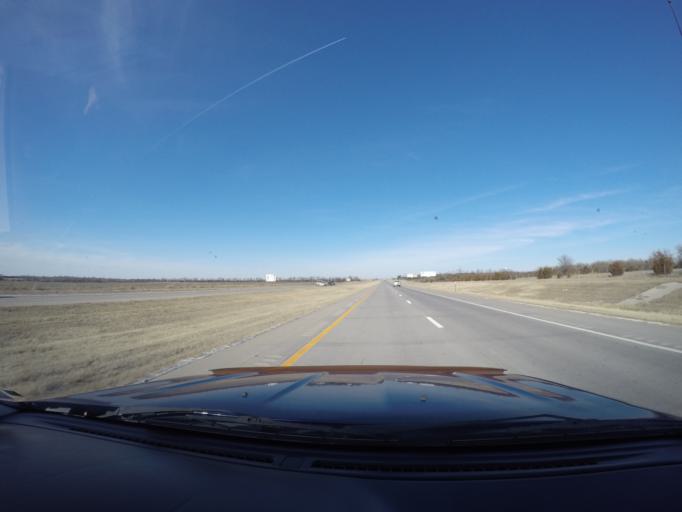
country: US
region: Kansas
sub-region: Sedgwick County
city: Valley Center
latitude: 37.8549
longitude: -97.3263
